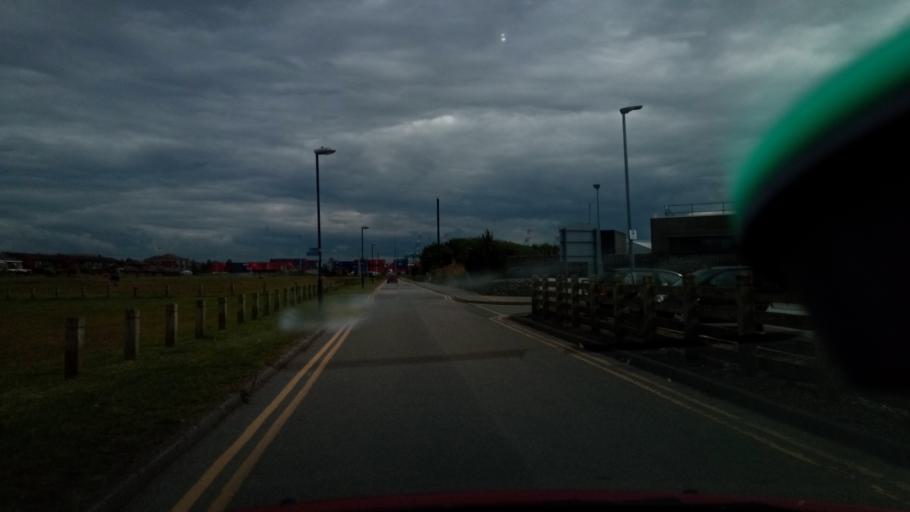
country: GB
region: England
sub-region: Sefton
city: Waterloo
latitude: 53.4711
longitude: -3.0291
